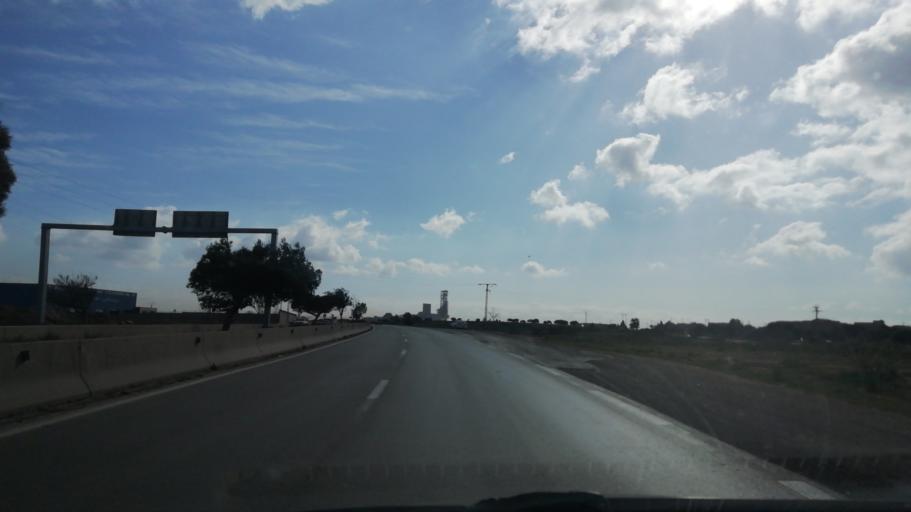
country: DZ
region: Oran
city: Ain el Bya
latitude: 35.7828
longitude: -0.2829
